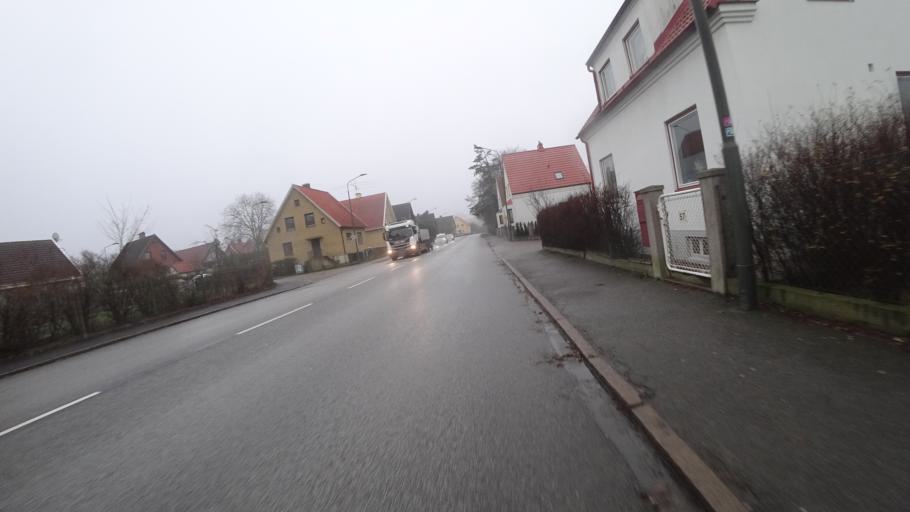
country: SE
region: Skane
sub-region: Malmo
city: Malmoe
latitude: 55.5715
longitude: 13.0132
